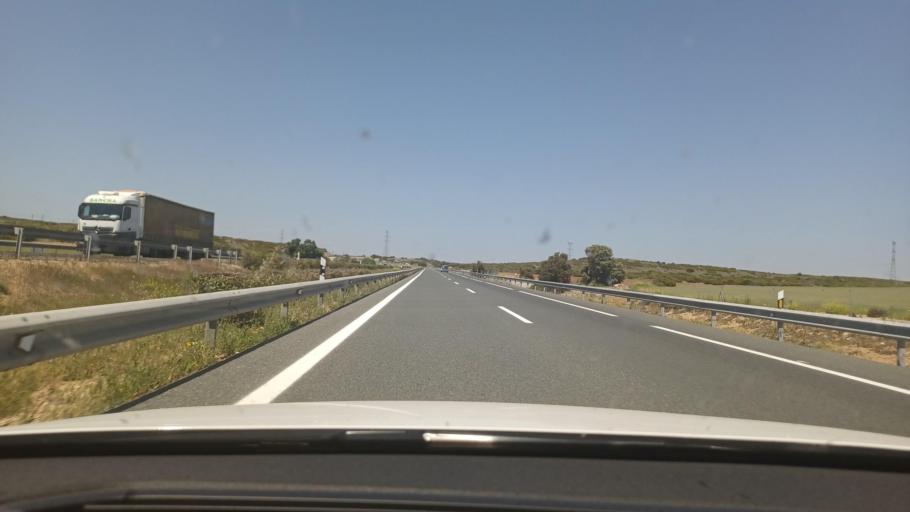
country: ES
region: Castille-La Mancha
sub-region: Provincia de Albacete
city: Alpera
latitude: 38.8795
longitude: -1.2423
